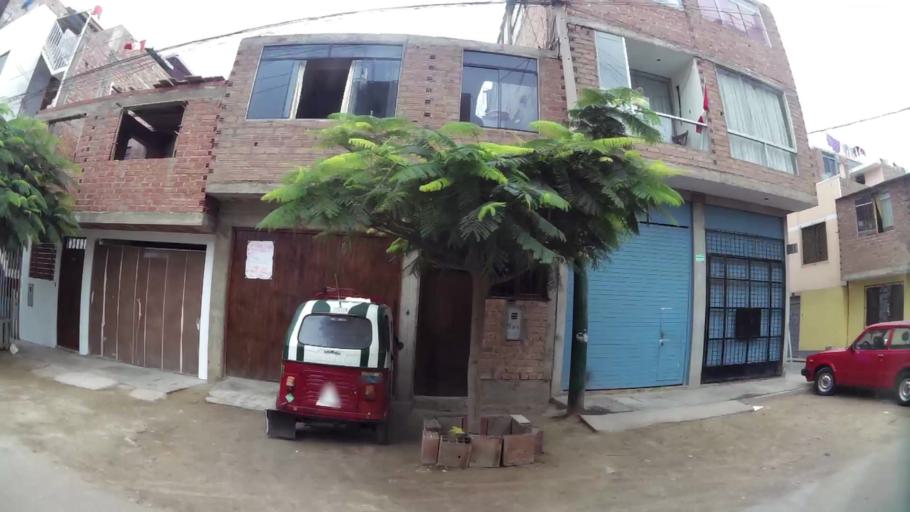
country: PE
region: Lima
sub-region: Lima
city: Surco
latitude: -12.1522
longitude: -77.0148
